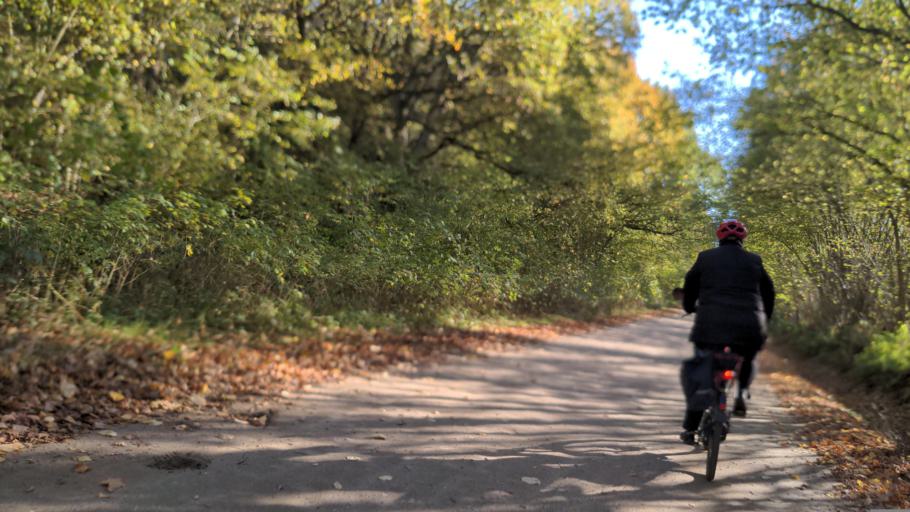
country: DE
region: Schleswig-Holstein
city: Ratekau
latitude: 53.9943
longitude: 10.6930
